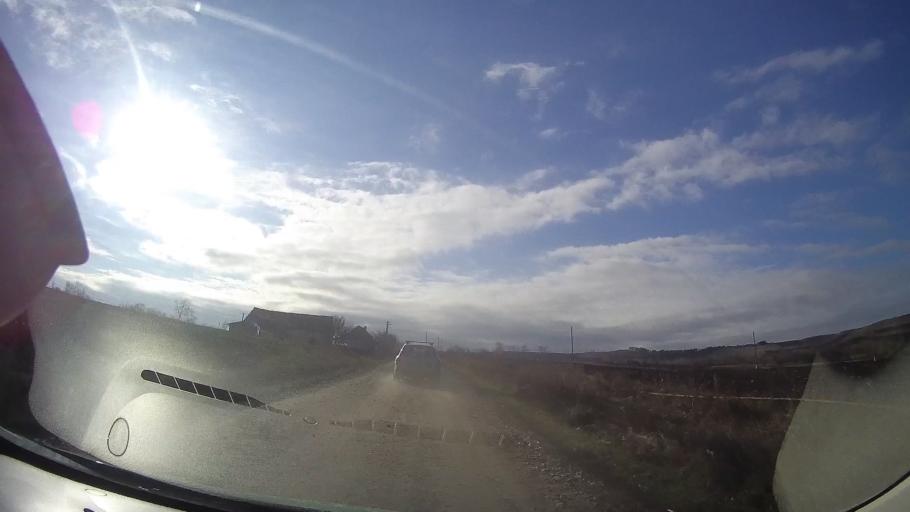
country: RO
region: Mures
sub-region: Comuna Papiu Ilarian
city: Papiu Ilarian
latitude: 46.5715
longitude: 24.2120
